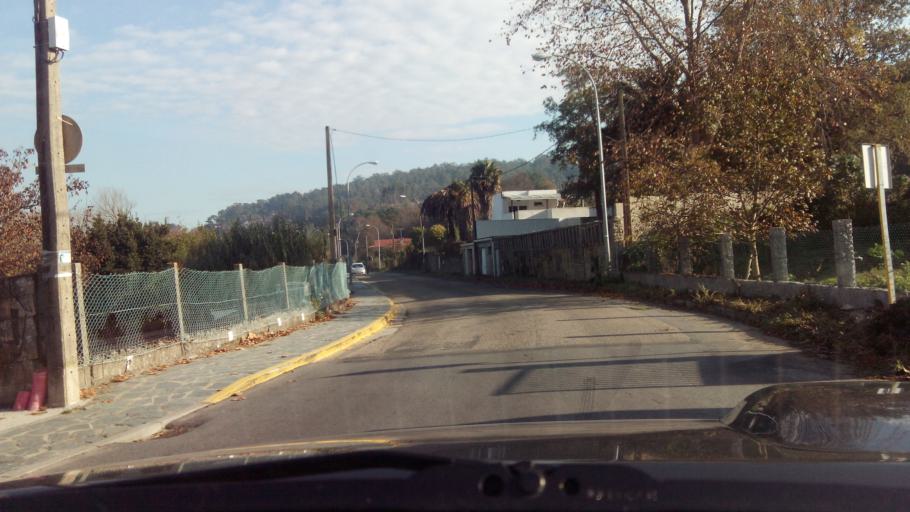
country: ES
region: Galicia
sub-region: Provincia de Pontevedra
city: Marin
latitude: 42.3727
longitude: -8.7339
